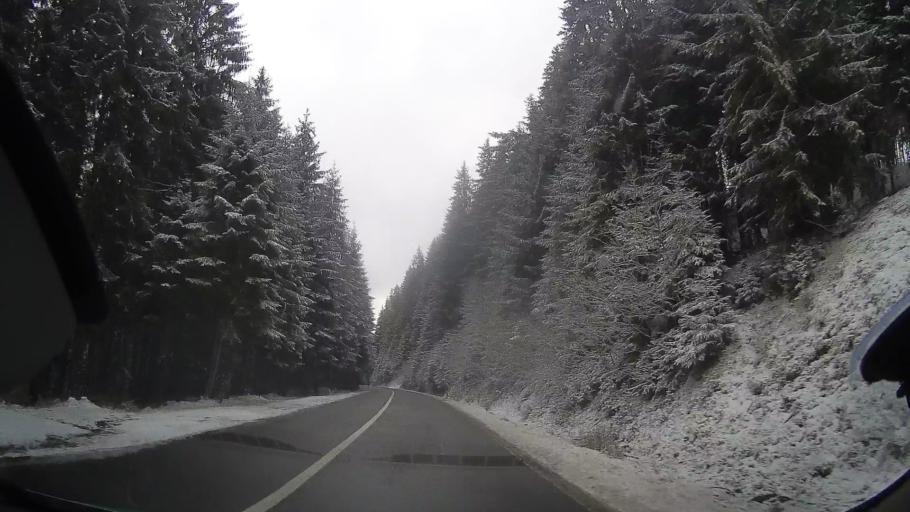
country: RO
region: Cluj
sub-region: Comuna Belis
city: Belis
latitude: 46.6523
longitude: 23.0528
